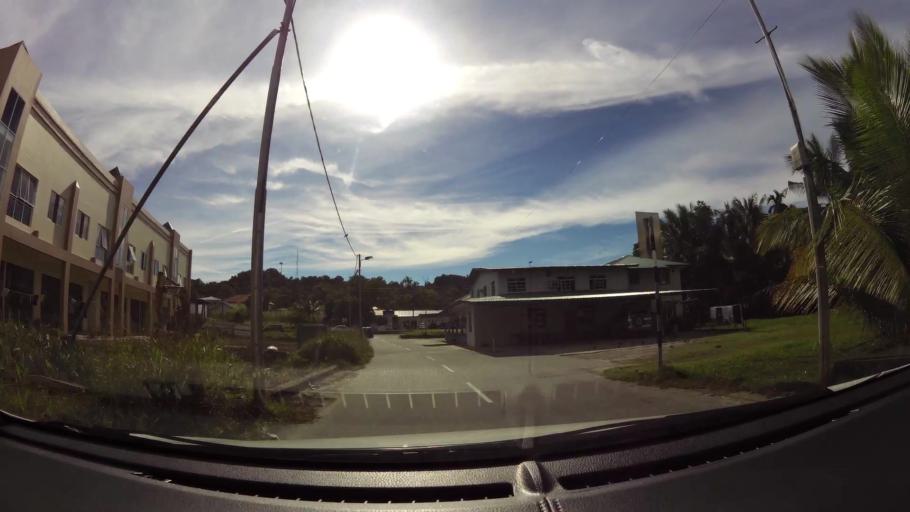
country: BN
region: Brunei and Muara
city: Bandar Seri Begawan
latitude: 4.9805
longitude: 115.0221
